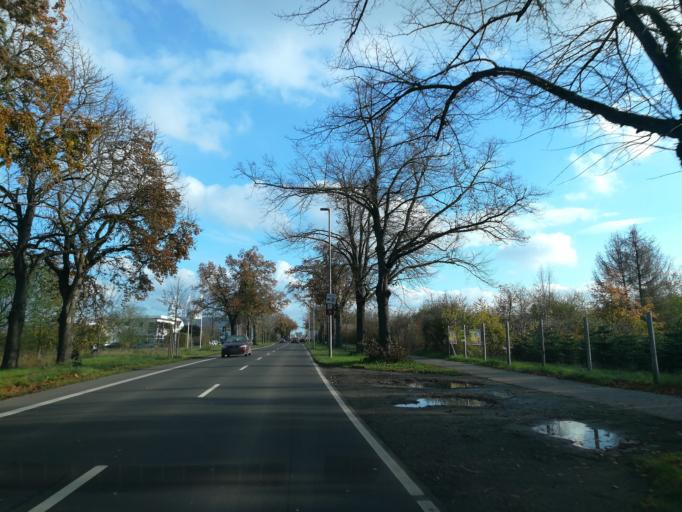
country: DE
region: Saxony-Anhalt
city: Haldensleben I
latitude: 52.2842
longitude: 11.4273
